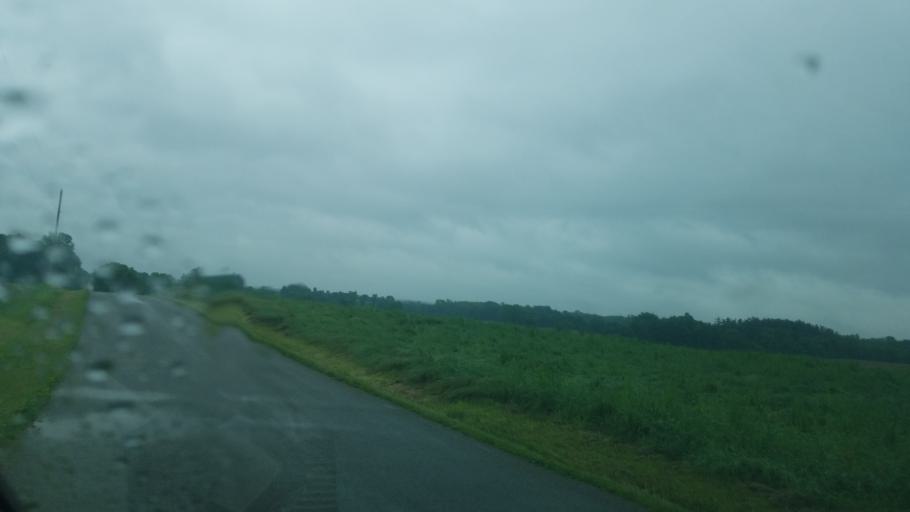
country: US
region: Ohio
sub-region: Richland County
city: Shelby
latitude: 40.9311
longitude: -82.5710
